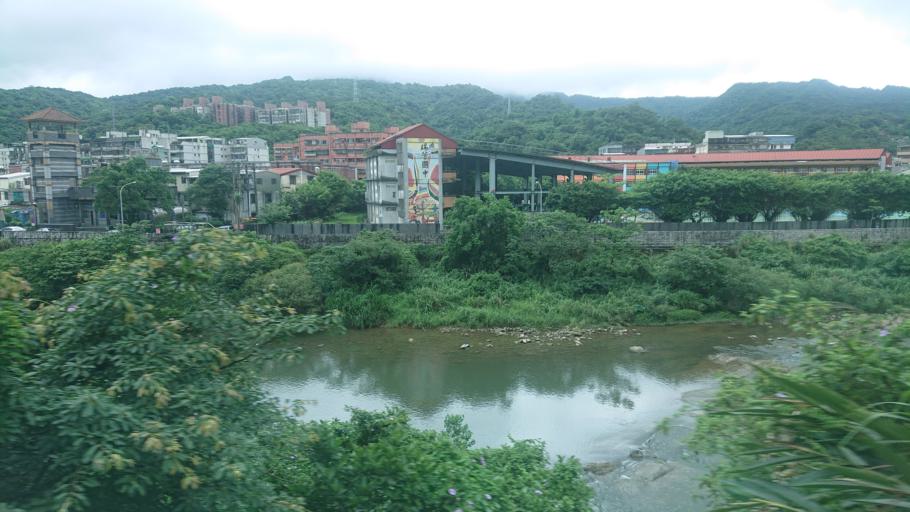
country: TW
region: Taiwan
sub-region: Keelung
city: Keelung
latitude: 25.1087
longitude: 121.8163
